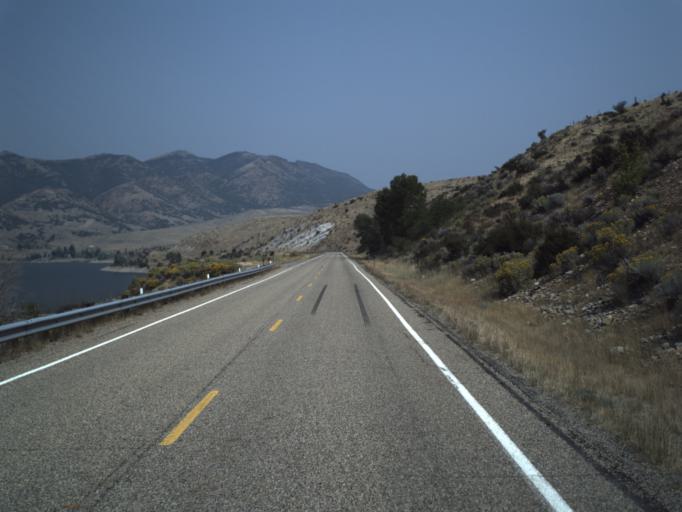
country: US
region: Utah
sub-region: Summit County
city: Summit Park
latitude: 40.9034
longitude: -111.5878
